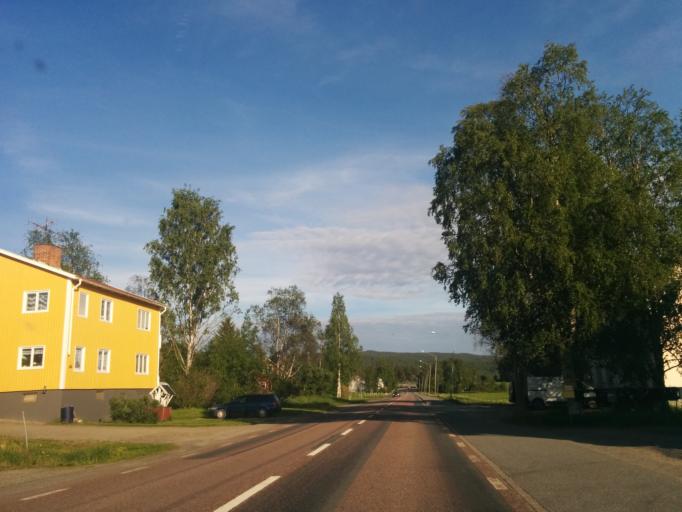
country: SE
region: Vaesternorrland
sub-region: Kramfors Kommun
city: Kramfors
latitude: 62.9720
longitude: 17.8867
